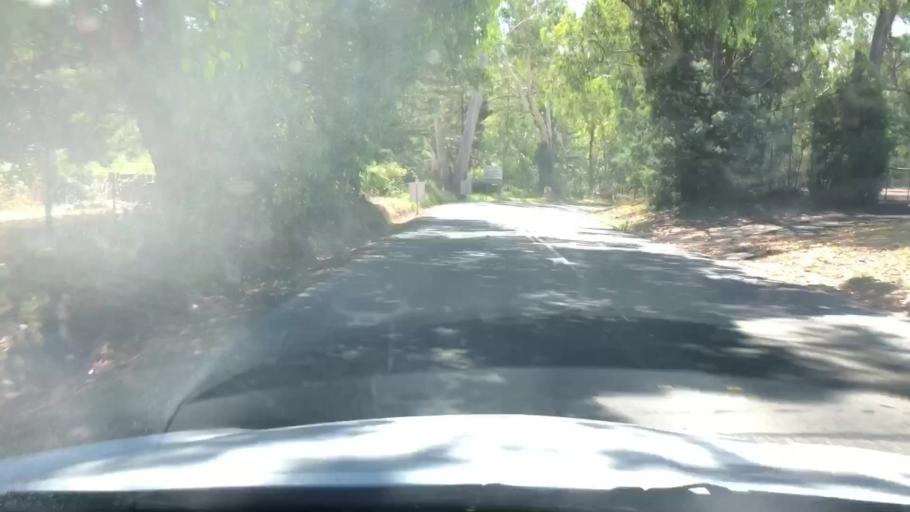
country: AU
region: Victoria
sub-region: Yarra Ranges
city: Woori Yallock
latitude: -37.8136
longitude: 145.5078
